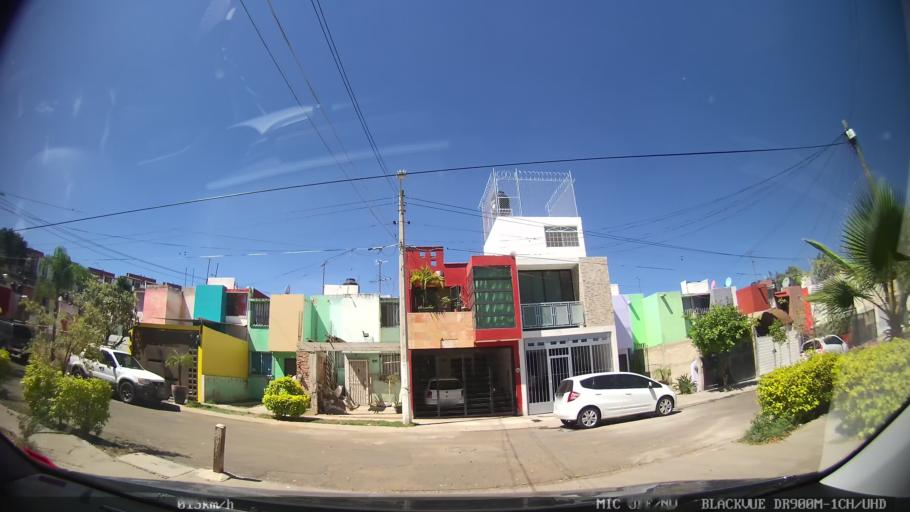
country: MX
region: Jalisco
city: Tlaquepaque
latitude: 20.6880
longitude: -103.2823
